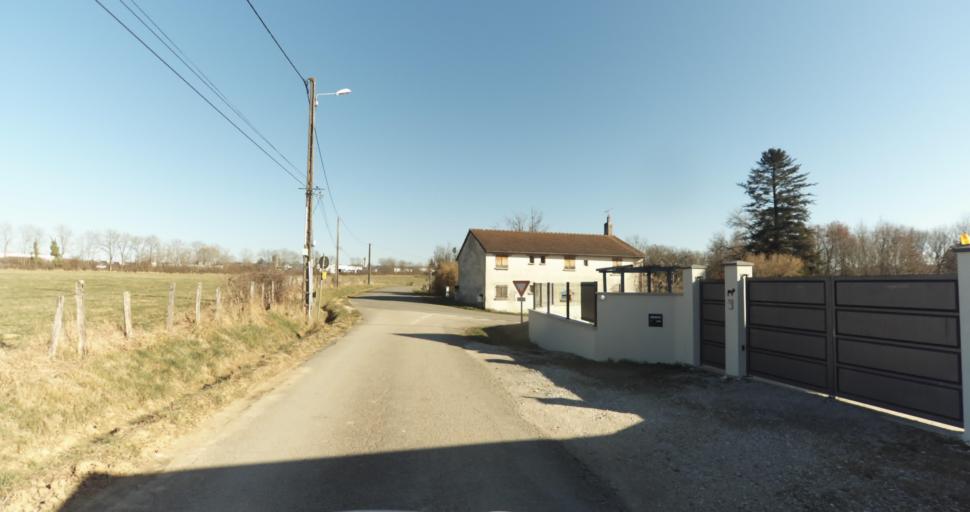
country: FR
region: Franche-Comte
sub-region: Departement du Jura
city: Montmorot
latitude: 46.6884
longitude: 5.4995
